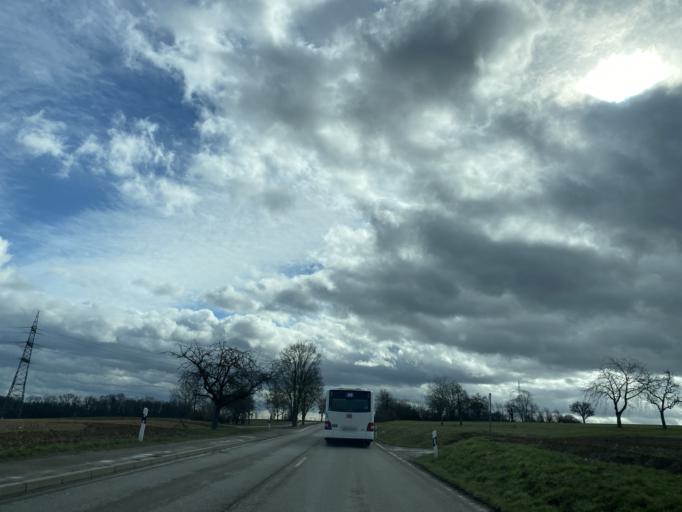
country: DE
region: Baden-Wuerttemberg
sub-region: Regierungsbezirk Stuttgart
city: Eberdingen
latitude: 48.8500
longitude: 8.9915
